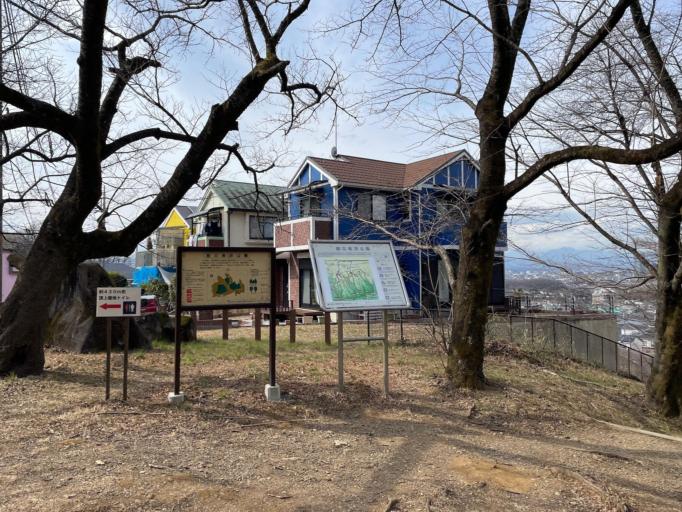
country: JP
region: Tokyo
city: Hachioji
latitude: 35.6351
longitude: 139.3651
